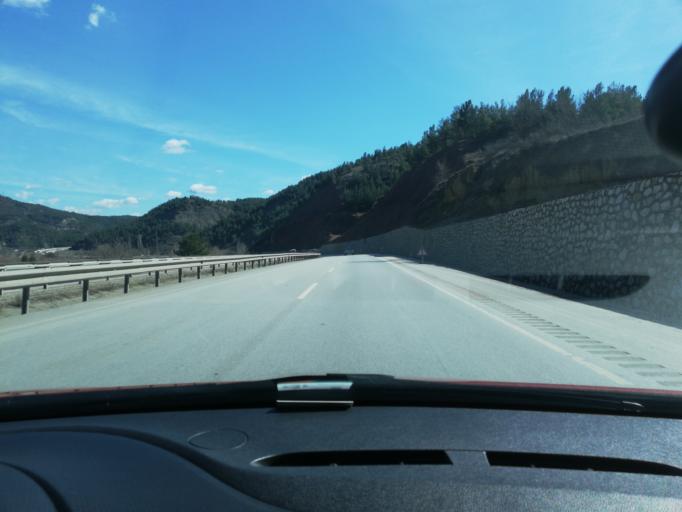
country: TR
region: Karabuk
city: Karabuk
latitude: 41.1534
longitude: 32.6544
